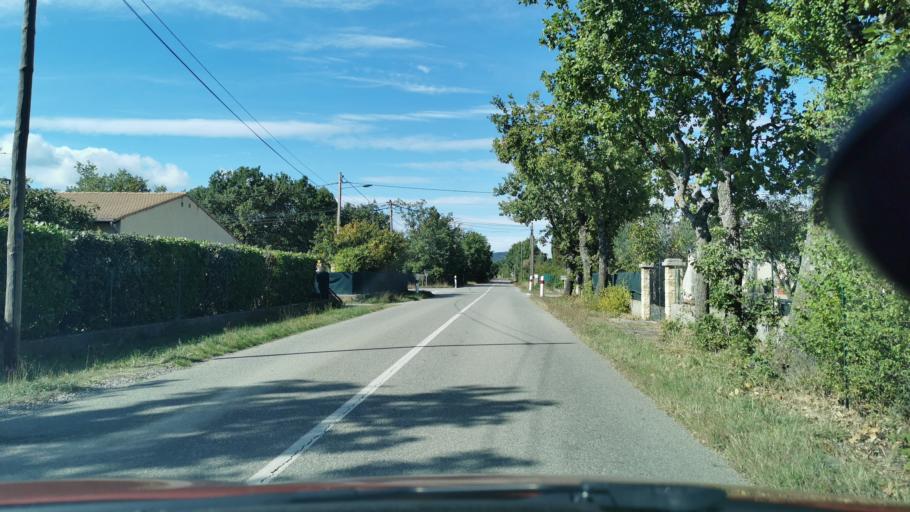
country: FR
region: Provence-Alpes-Cote d'Azur
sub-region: Departement des Alpes-de-Haute-Provence
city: Peipin
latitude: 44.1527
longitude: 5.9754
